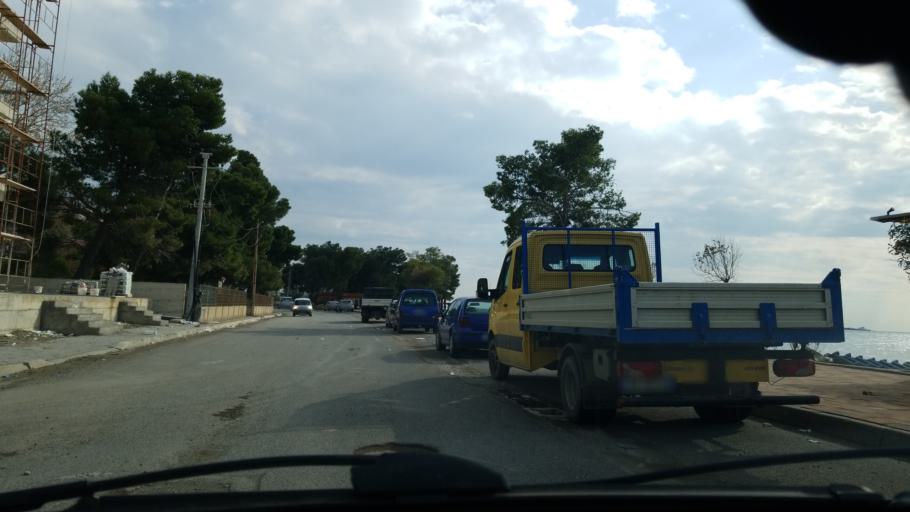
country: AL
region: Lezhe
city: Shengjin
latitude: 41.7956
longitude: 19.6020
